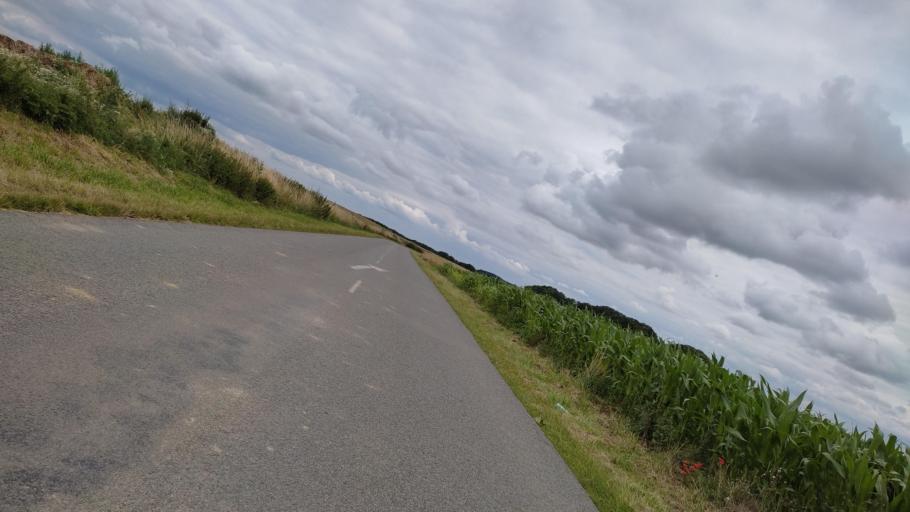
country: FR
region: Nord-Pas-de-Calais
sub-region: Departement du Pas-de-Calais
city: Beaumetz-les-Loges
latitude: 50.2386
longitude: 2.6715
